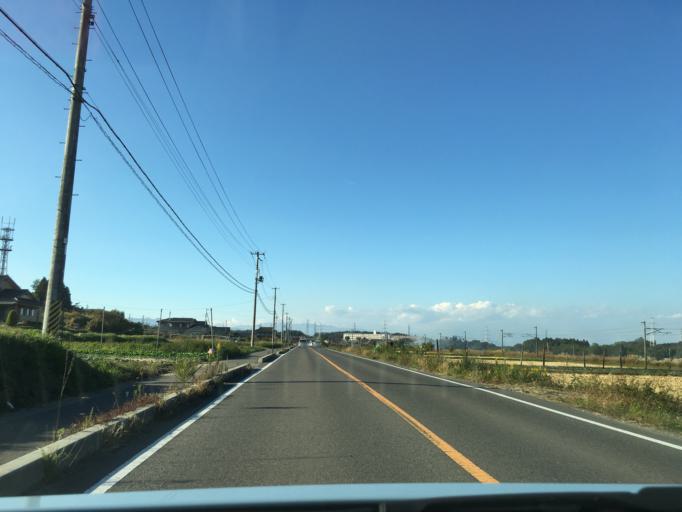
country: JP
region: Fukushima
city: Sukagawa
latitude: 37.3220
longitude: 140.3771
